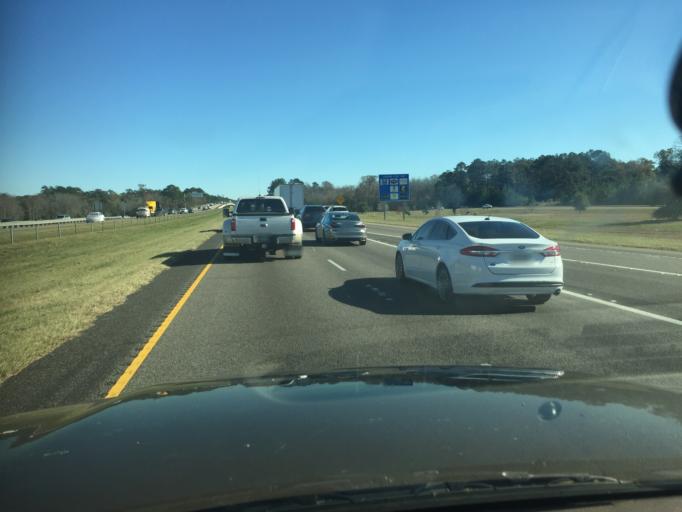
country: US
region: Louisiana
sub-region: Saint Tammany Parish
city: Covington
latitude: 30.4410
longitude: -90.1229
